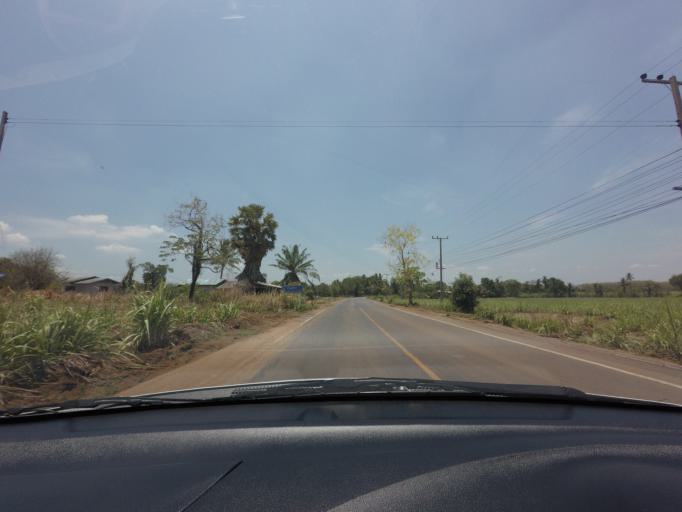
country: TH
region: Suphan Buri
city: Dan Chang
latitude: 14.8800
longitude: 99.7035
